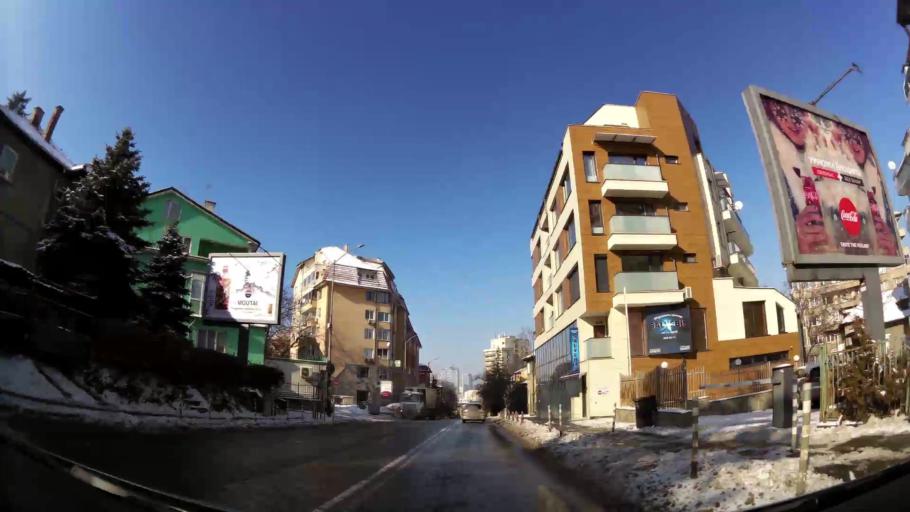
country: BG
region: Sofia-Capital
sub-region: Stolichna Obshtina
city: Sofia
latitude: 42.6769
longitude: 23.3328
